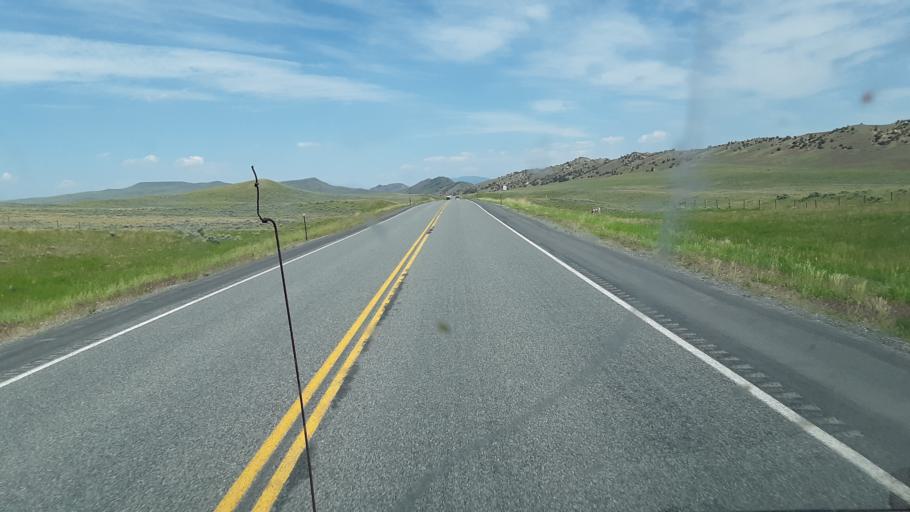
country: US
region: Wyoming
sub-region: Park County
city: Cody
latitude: 44.2873
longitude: -108.9008
